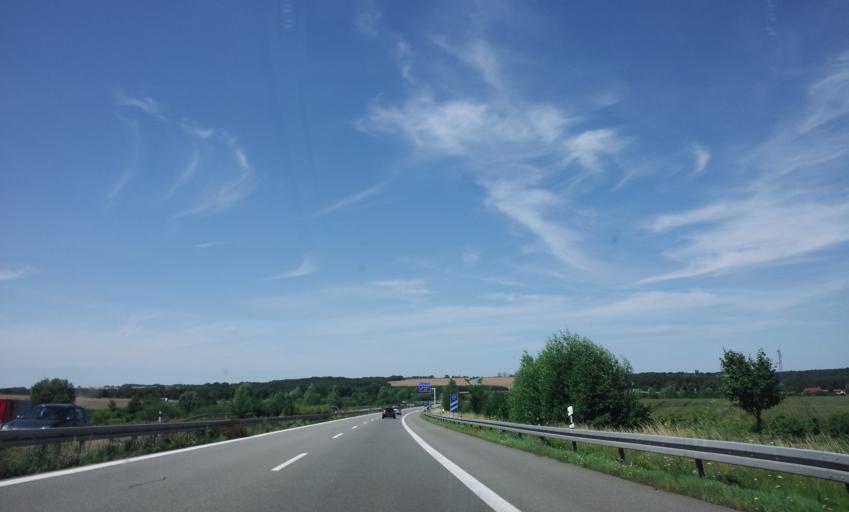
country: DE
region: Mecklenburg-Vorpommern
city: Neuenkirchen
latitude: 53.5785
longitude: 13.4299
